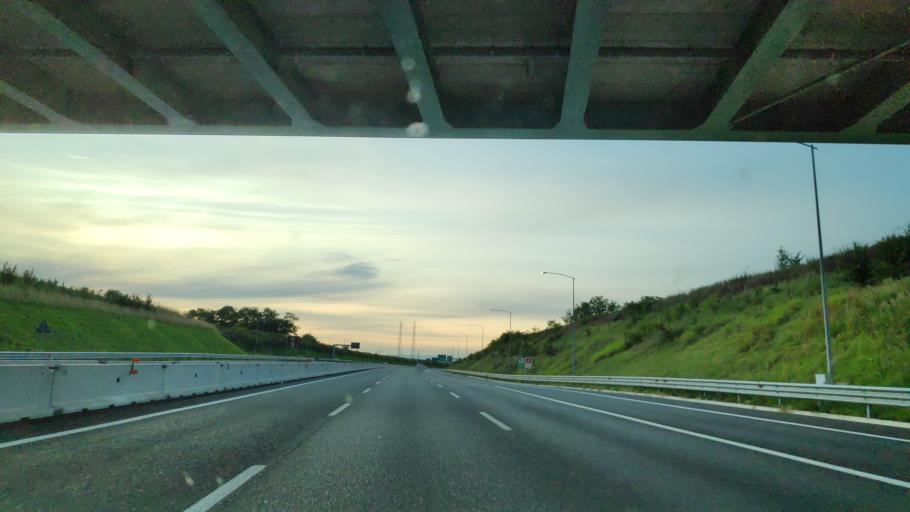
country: IT
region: Lombardy
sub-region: Citta metropolitana di Milano
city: Torrazza dei Mandelli
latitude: 45.5614
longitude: 9.3983
